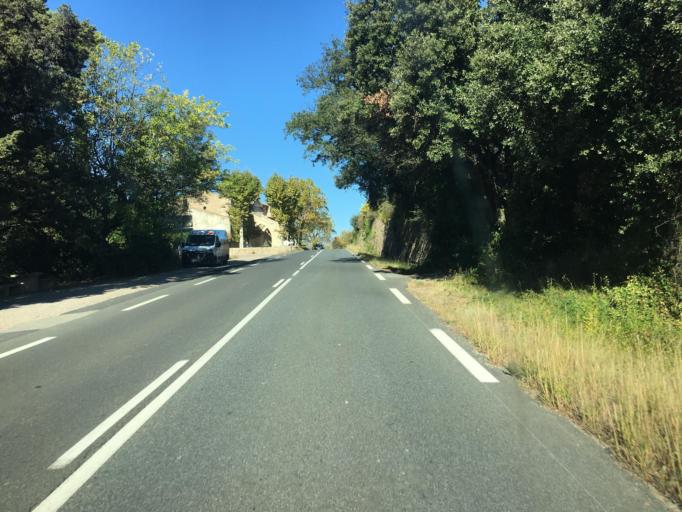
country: FR
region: Languedoc-Roussillon
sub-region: Departement de l'Herault
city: Nebian
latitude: 43.6183
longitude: 3.4104
